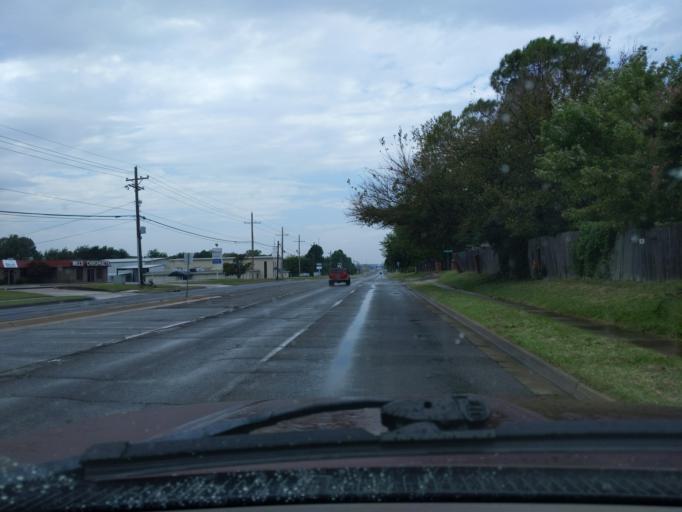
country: US
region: Oklahoma
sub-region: Tulsa County
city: Broken Arrow
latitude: 36.1335
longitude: -95.8365
